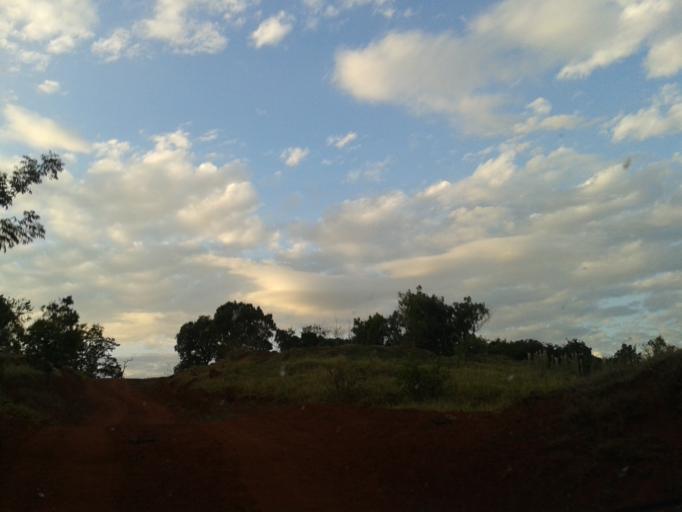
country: BR
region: Minas Gerais
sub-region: Campina Verde
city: Campina Verde
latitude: -19.3487
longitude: -49.6628
